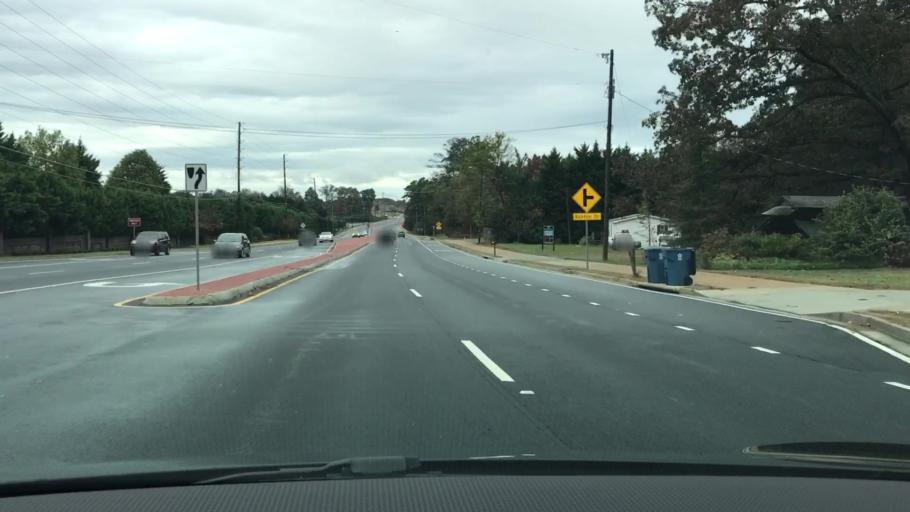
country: US
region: Georgia
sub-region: Gwinnett County
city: Suwanee
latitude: 34.1071
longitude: -84.1459
